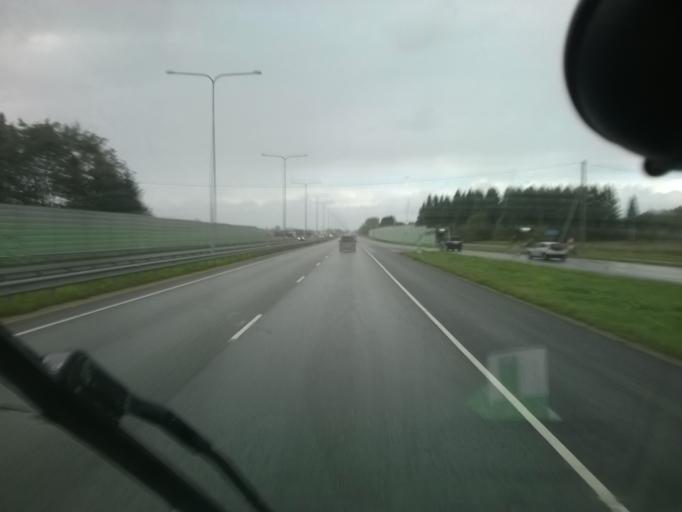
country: EE
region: Harju
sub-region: Rae vald
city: Jueri
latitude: 59.3847
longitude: 24.8351
